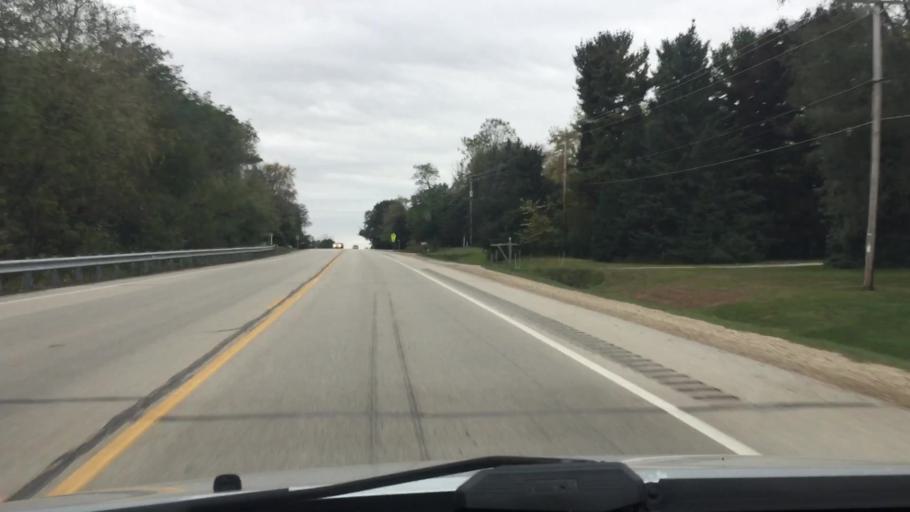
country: US
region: Wisconsin
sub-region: Waukesha County
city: Waukesha
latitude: 42.9769
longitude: -88.2881
